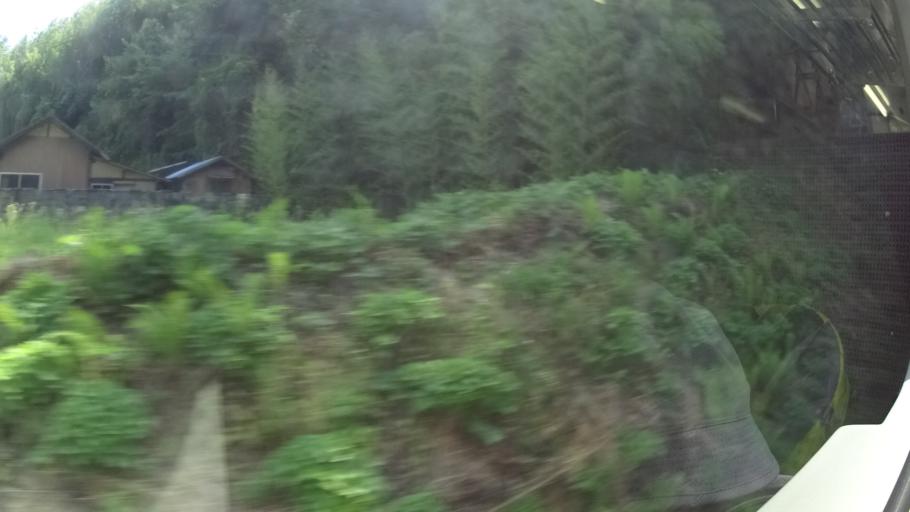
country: JP
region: Miyagi
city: Wakuya
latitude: 38.5171
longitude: 141.1795
